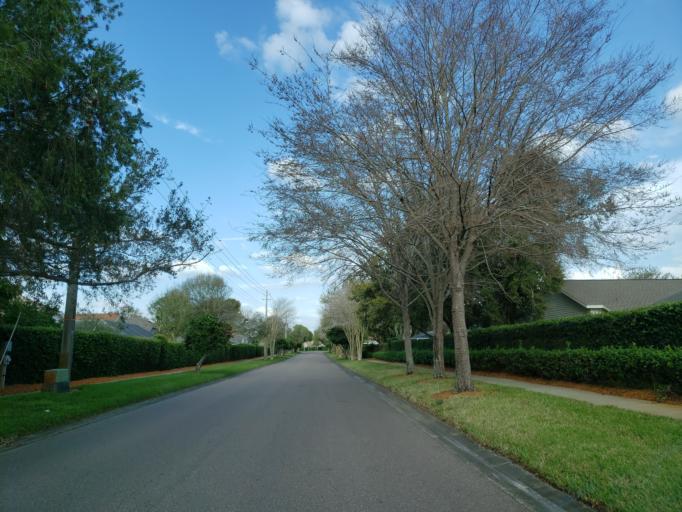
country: US
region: Florida
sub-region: Hillsborough County
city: Brandon
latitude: 27.9086
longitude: -82.3146
